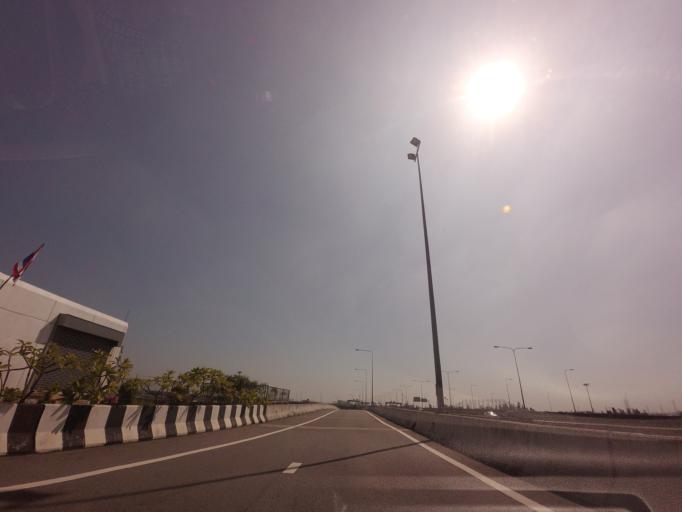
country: TH
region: Bangkok
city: Bang Na
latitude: 13.6486
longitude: 100.6848
